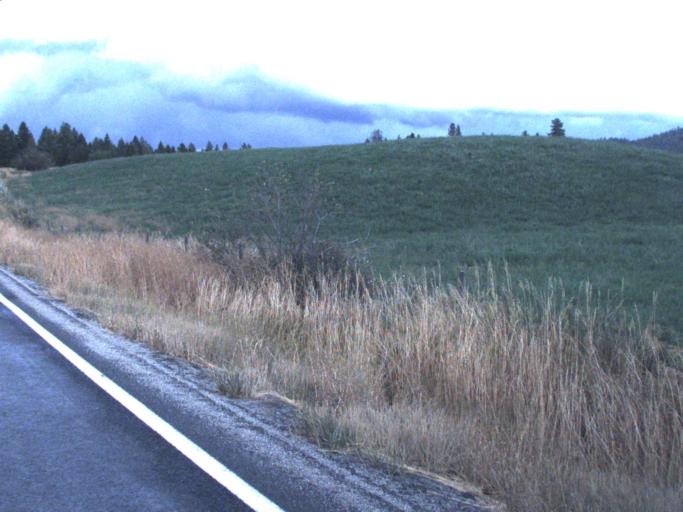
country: US
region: Washington
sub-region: Stevens County
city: Chewelah
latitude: 48.1036
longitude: -117.7578
